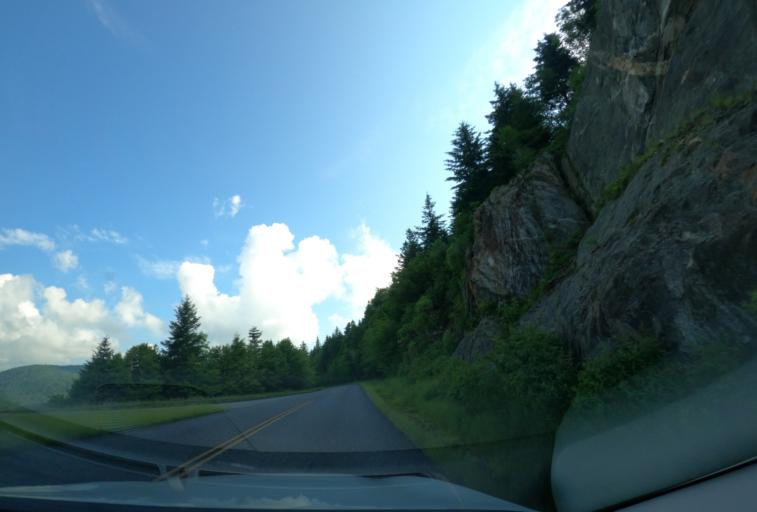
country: US
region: North Carolina
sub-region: Haywood County
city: Hazelwood
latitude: 35.3275
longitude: -82.9650
